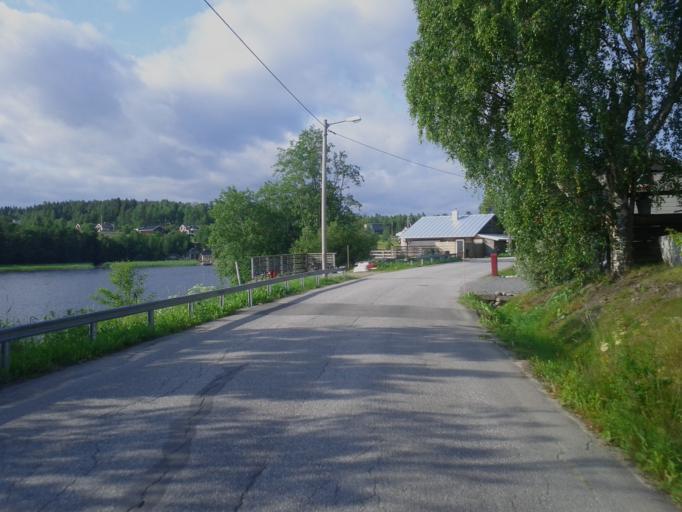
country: SE
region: Vaesternorrland
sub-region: OErnskoeldsviks Kommun
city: Ornskoldsvik
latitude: 63.2676
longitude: 18.8061
